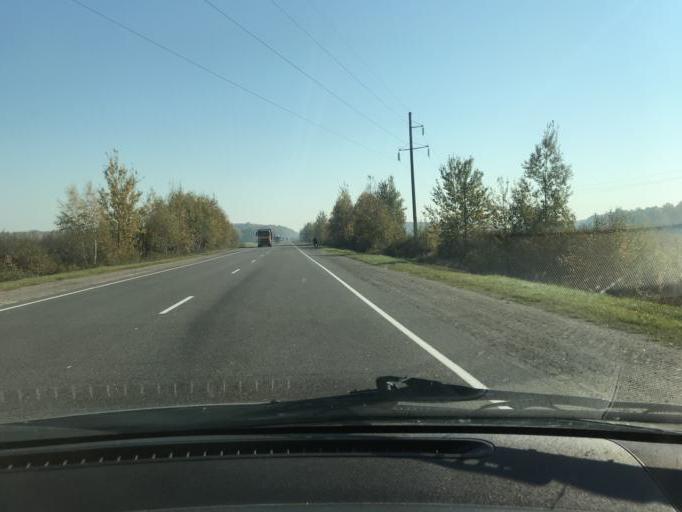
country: BY
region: Brest
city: Horad Luninyets
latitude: 52.3125
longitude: 26.6591
